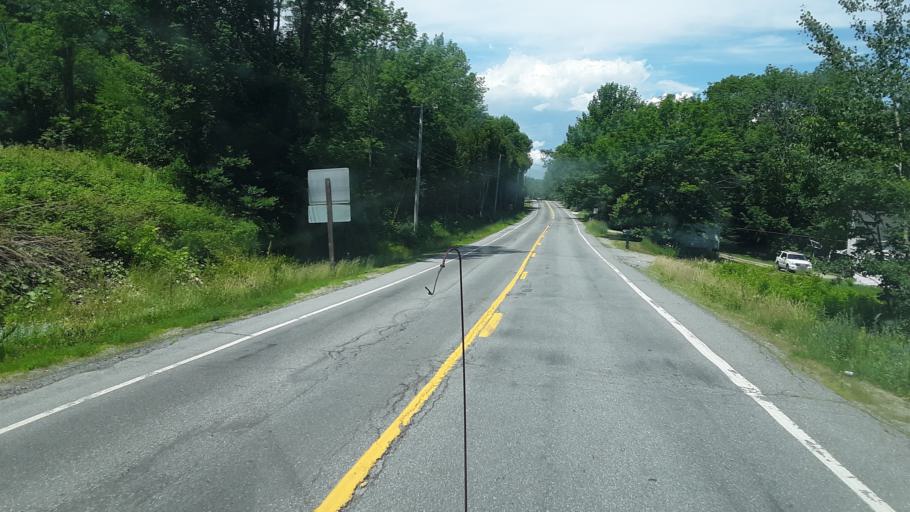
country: US
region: Maine
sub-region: Hancock County
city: Bucksport
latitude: 44.5675
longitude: -68.8060
